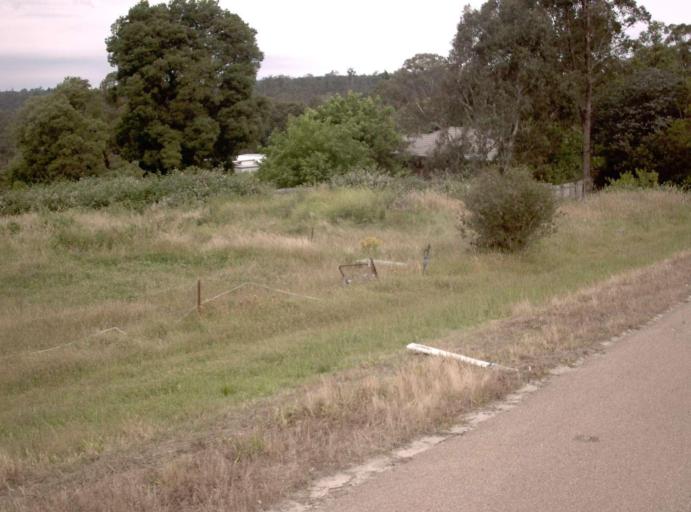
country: AU
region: Victoria
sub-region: East Gippsland
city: Lakes Entrance
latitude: -37.7288
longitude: 148.0888
